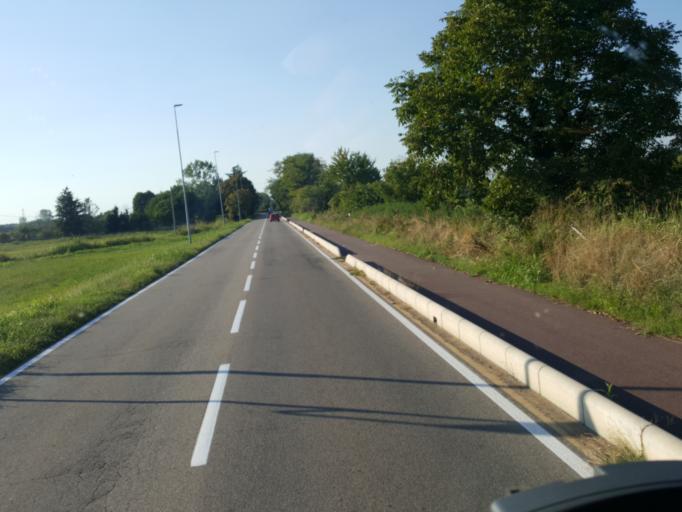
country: IT
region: Lombardy
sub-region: Citta metropolitana di Milano
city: Parabiago
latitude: 45.5658
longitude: 8.9552
